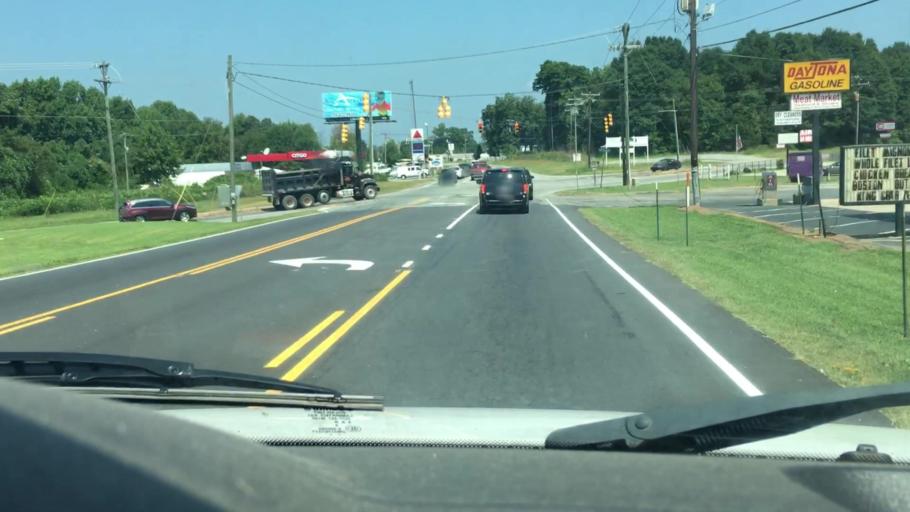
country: US
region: North Carolina
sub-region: Lincoln County
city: Westport
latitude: 35.4781
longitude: -80.9934
